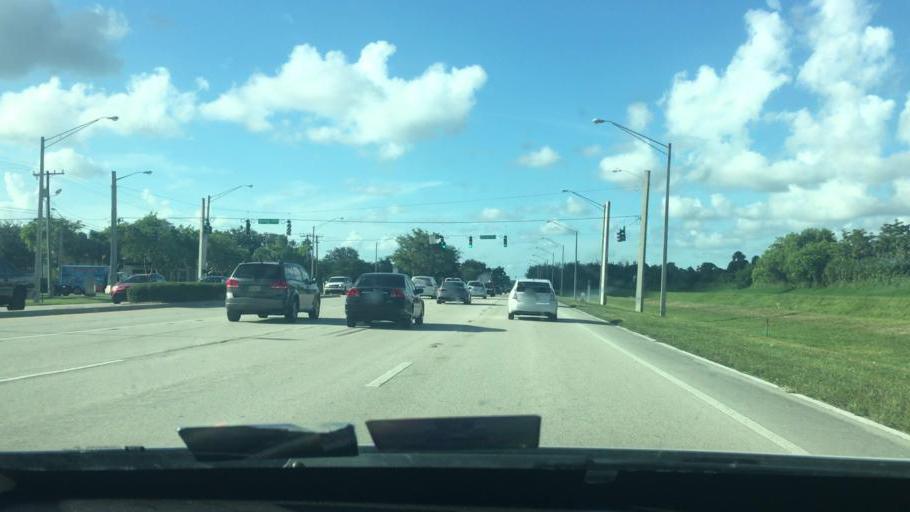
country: US
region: Florida
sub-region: Palm Beach County
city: Royal Palm Beach
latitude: 26.6985
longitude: -80.2012
